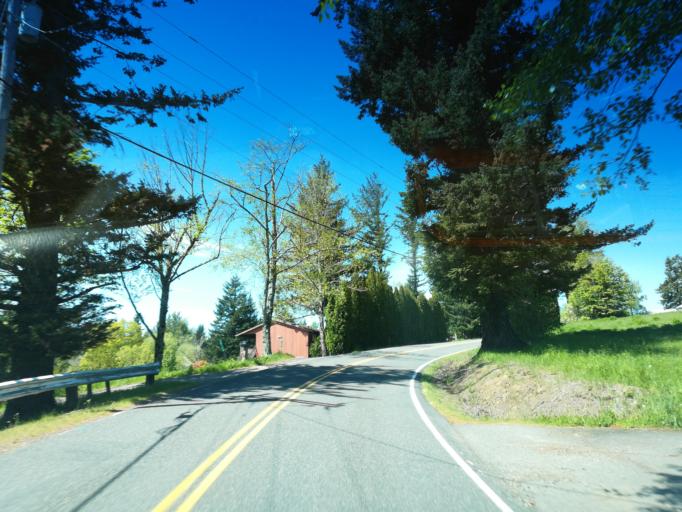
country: US
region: Oregon
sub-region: Multnomah County
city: Troutdale
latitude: 45.5211
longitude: -122.3520
